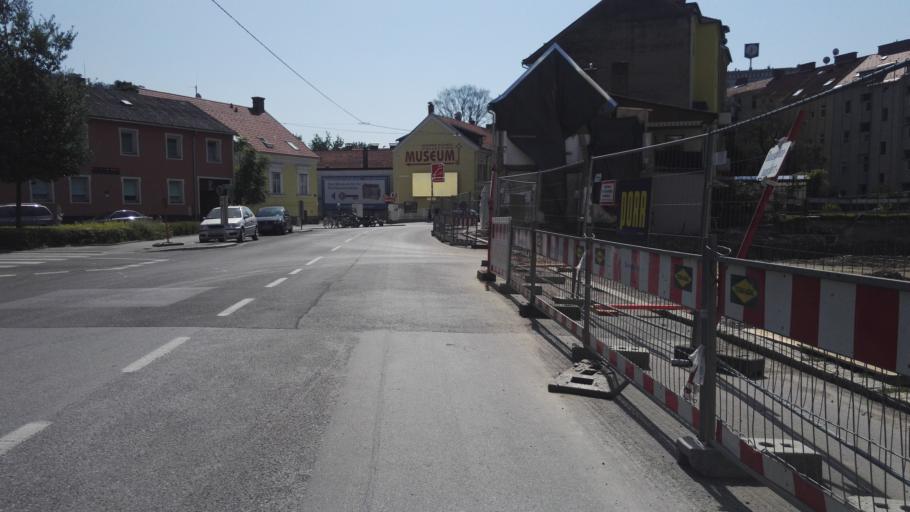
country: AT
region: Styria
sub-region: Graz Stadt
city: Graz
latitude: 47.0784
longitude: 15.4277
